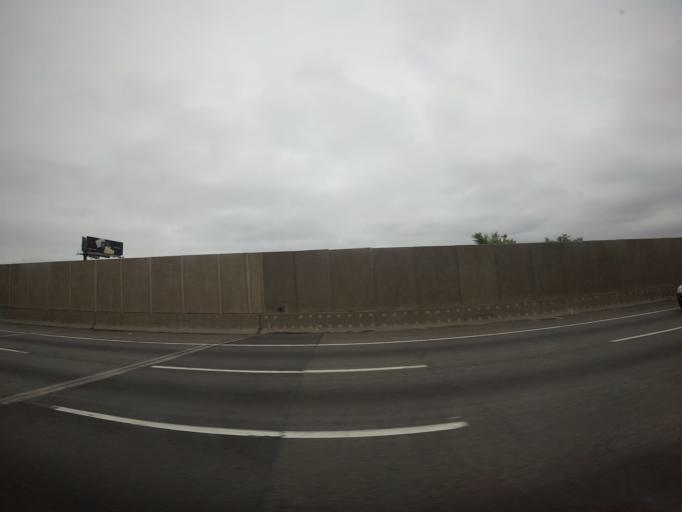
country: US
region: New Jersey
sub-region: Union County
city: Elizabeth
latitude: 40.6562
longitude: -74.1886
